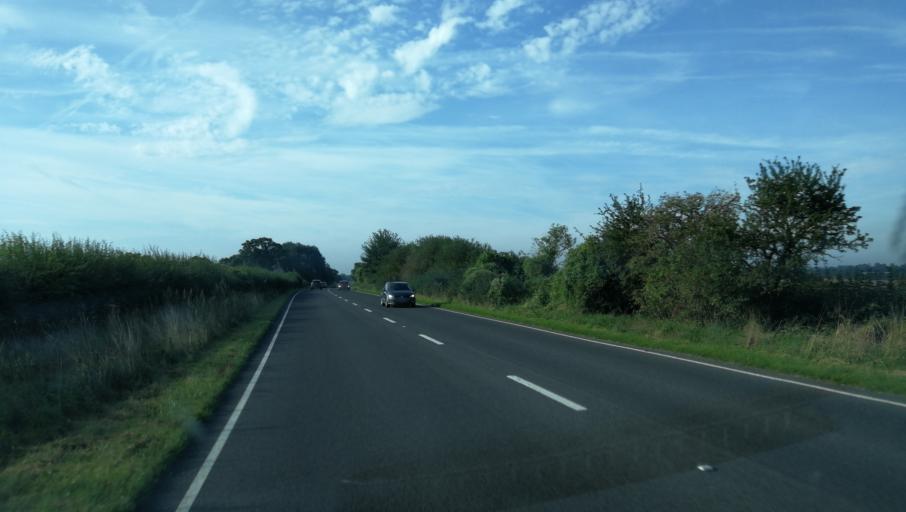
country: GB
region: England
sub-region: Oxfordshire
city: Woodstock
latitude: 51.8864
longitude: -1.3281
